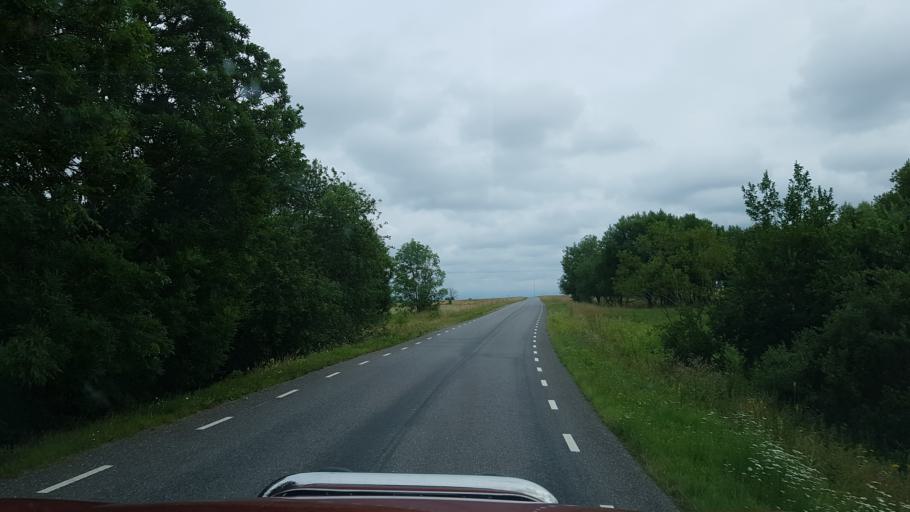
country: EE
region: Ida-Virumaa
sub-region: Puessi linn
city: Pussi
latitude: 59.3967
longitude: 27.0171
